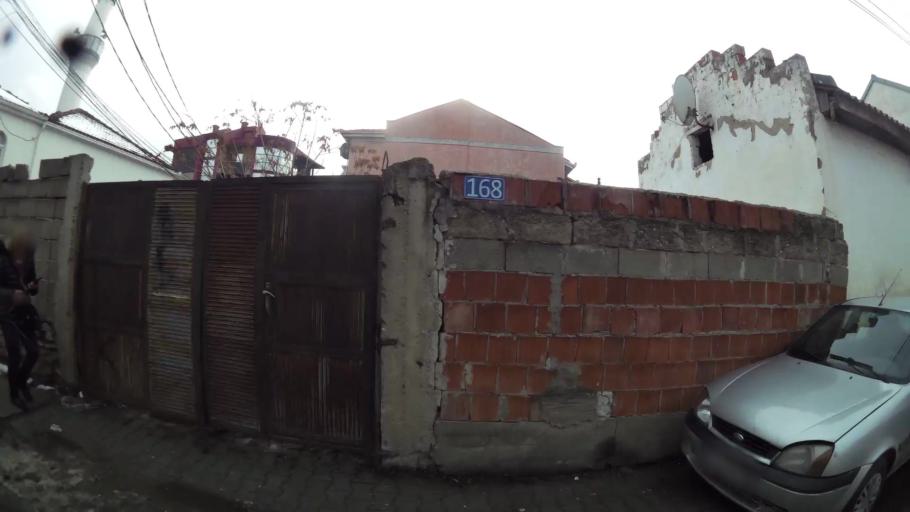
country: XK
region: Pristina
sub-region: Komuna e Prishtines
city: Pristina
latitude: 42.6713
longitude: 21.1685
